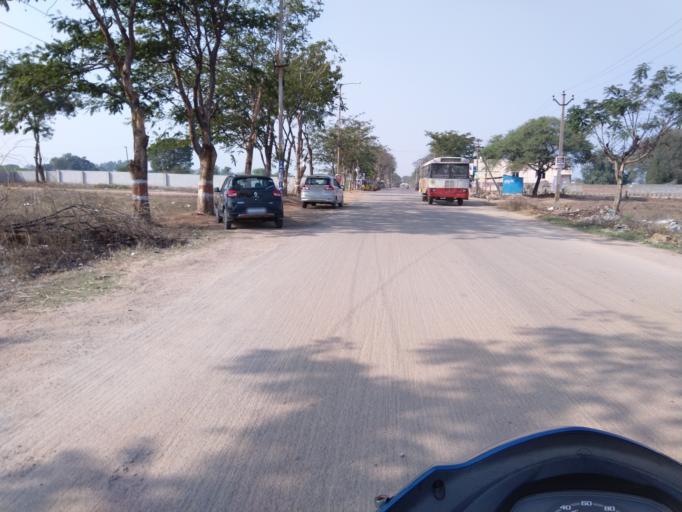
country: IN
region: Telangana
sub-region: Rangareddi
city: Quthbullapur
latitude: 17.5980
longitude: 78.4164
